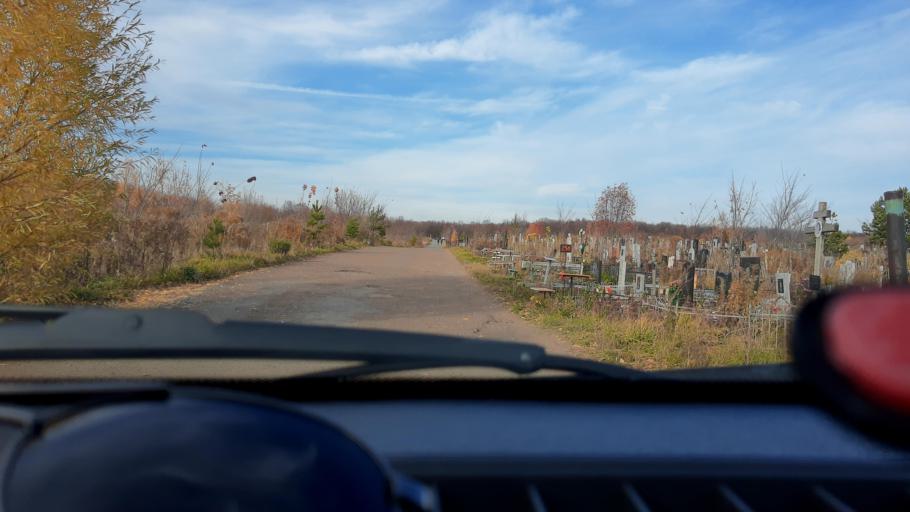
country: RU
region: Bashkortostan
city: Ufa
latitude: 54.8593
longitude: 56.1573
